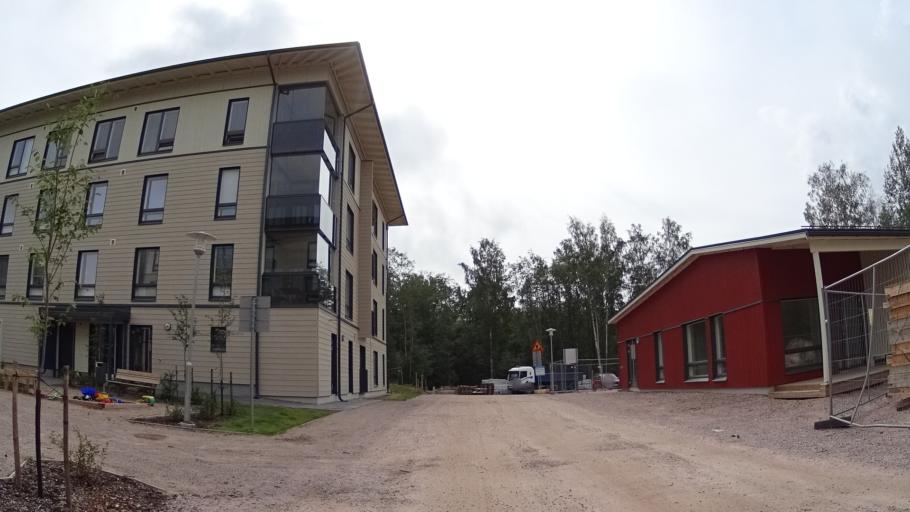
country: FI
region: Uusimaa
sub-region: Helsinki
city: Kilo
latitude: 60.2209
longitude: 24.7870
